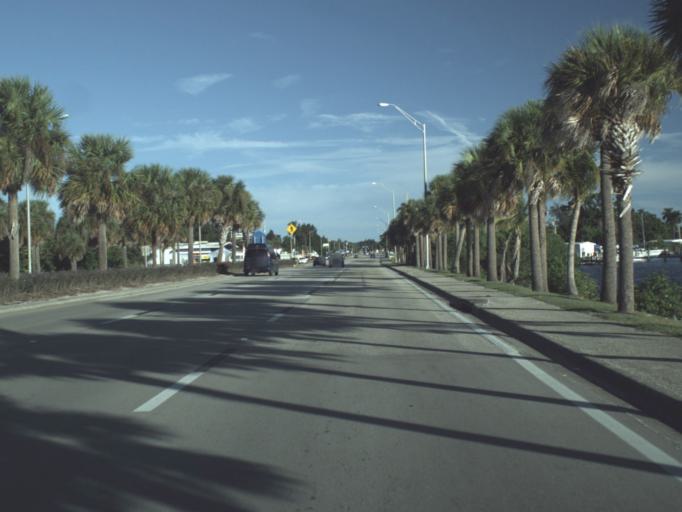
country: US
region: Florida
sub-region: Lee County
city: North Fort Myers
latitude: 26.6608
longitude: -81.8757
